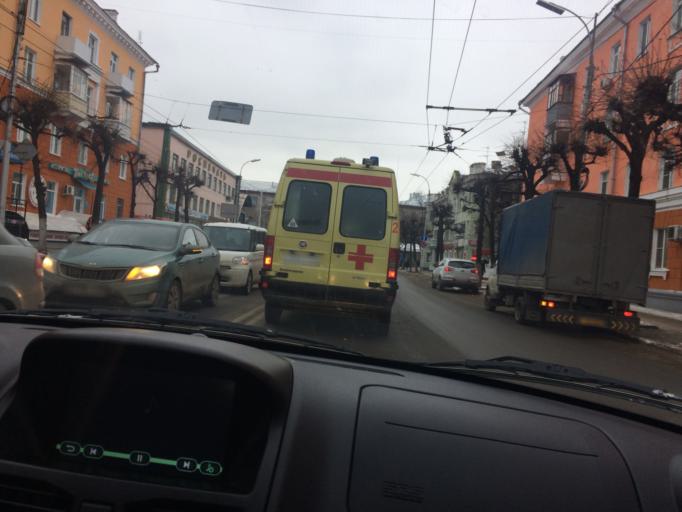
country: RU
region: Rjazan
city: Ryazan'
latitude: 54.6289
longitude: 39.7162
